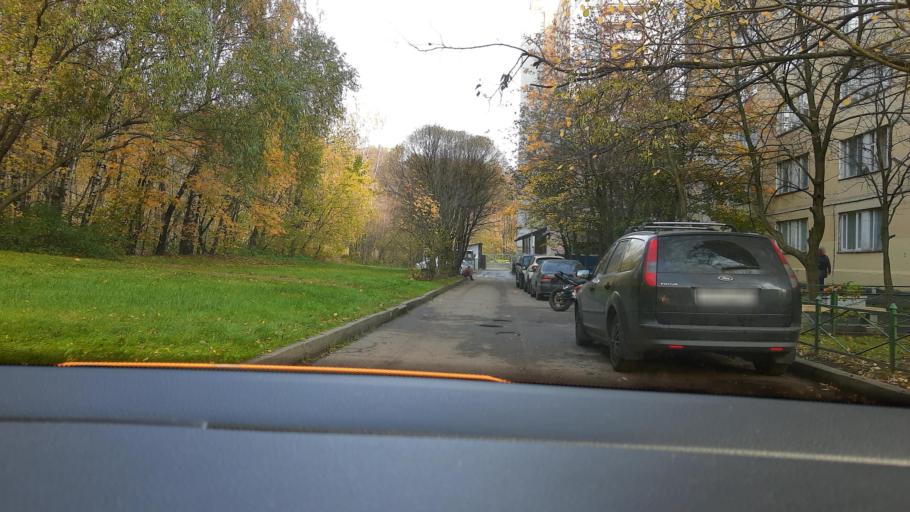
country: RU
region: Moscow
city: Khimki
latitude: 55.8640
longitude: 37.4194
